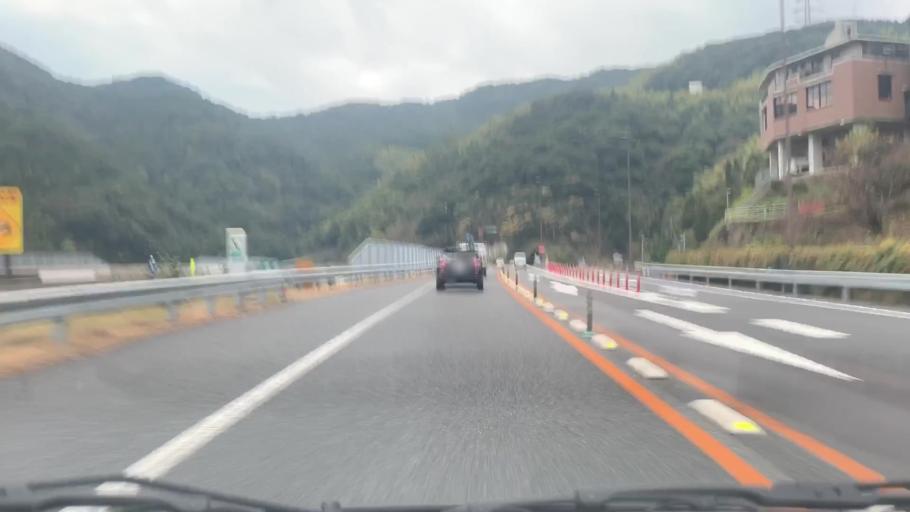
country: JP
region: Nagasaki
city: Nagasaki-shi
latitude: 32.7536
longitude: 129.9281
